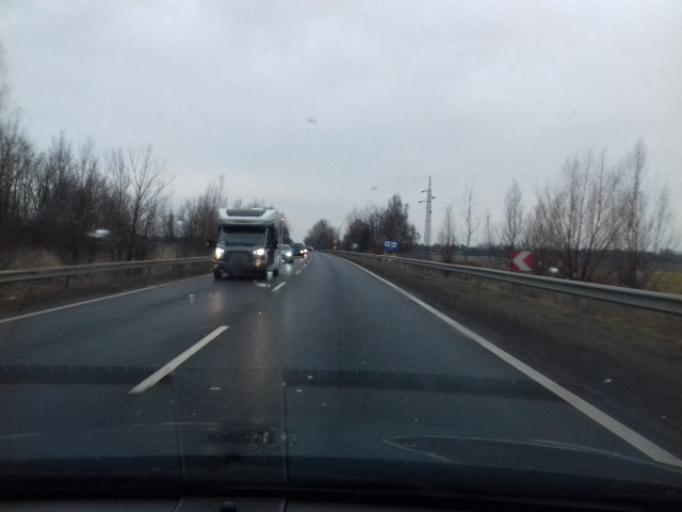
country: HU
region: Szabolcs-Szatmar-Bereg
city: Ujfeherto
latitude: 47.8752
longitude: 21.7058
